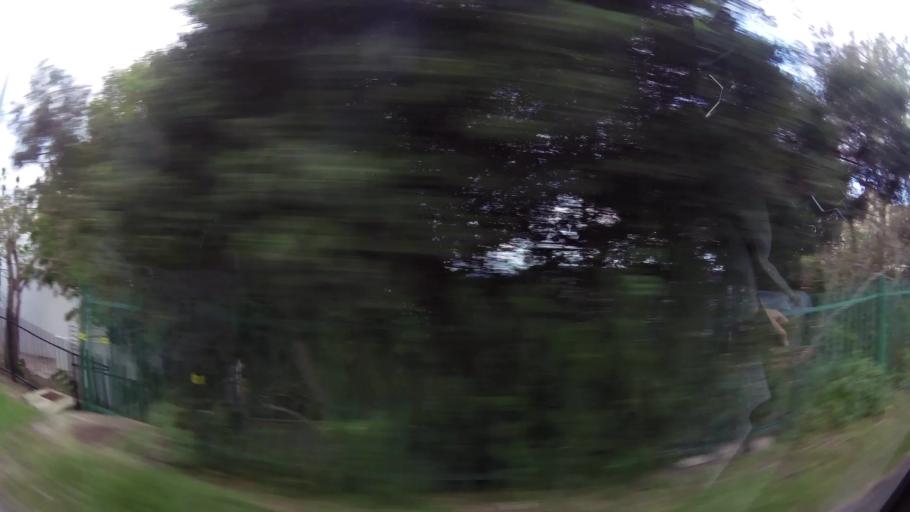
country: ZA
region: Western Cape
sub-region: Eden District Municipality
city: Plettenberg Bay
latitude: -34.0475
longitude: 23.3652
